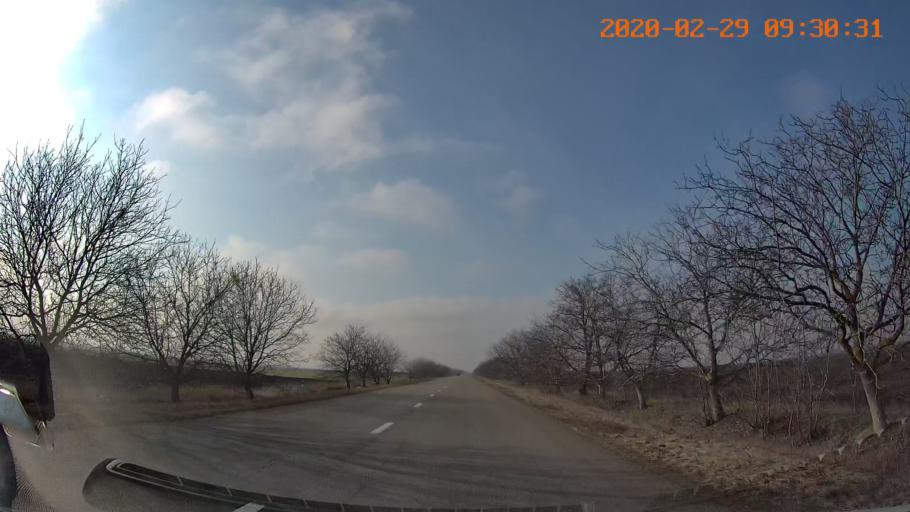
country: MD
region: Telenesti
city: Dnestrovsc
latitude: 46.6654
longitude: 29.9161
